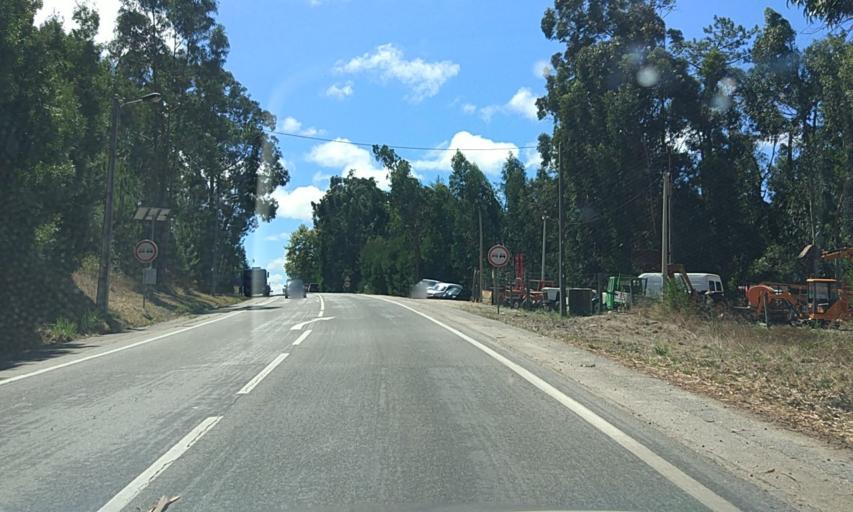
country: PT
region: Aveiro
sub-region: Vagos
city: Vagos
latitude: 40.5064
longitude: -8.6789
